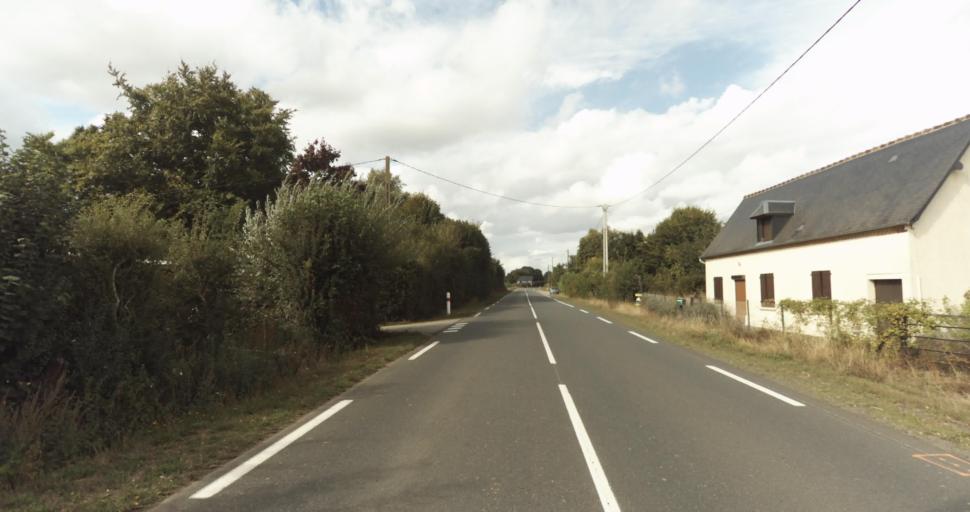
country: FR
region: Lower Normandy
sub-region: Departement de l'Orne
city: Gace
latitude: 48.8563
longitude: 0.2537
